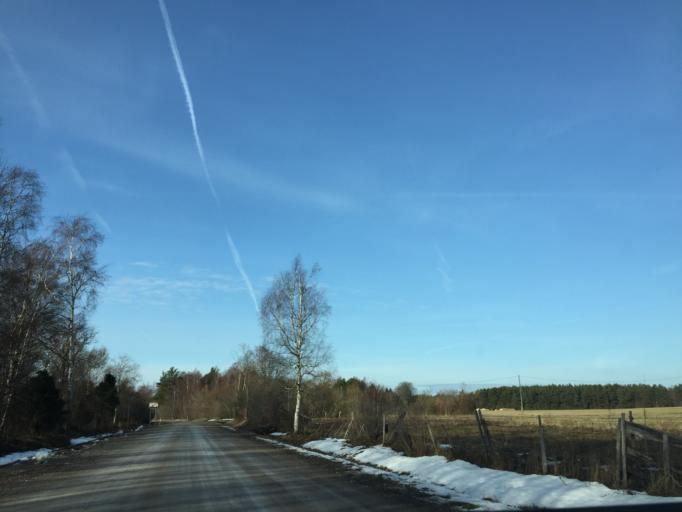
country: EE
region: Saare
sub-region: Kuressaare linn
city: Kuressaare
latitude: 58.3666
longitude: 22.0316
